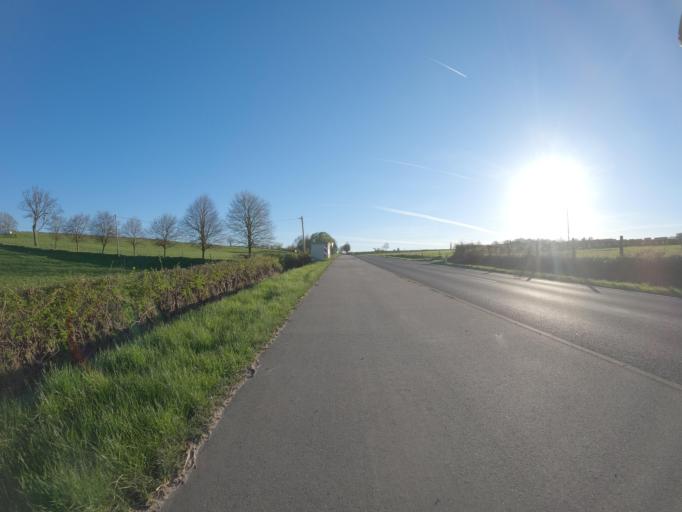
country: DE
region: North Rhine-Westphalia
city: Stolberg
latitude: 50.7779
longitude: 6.2597
